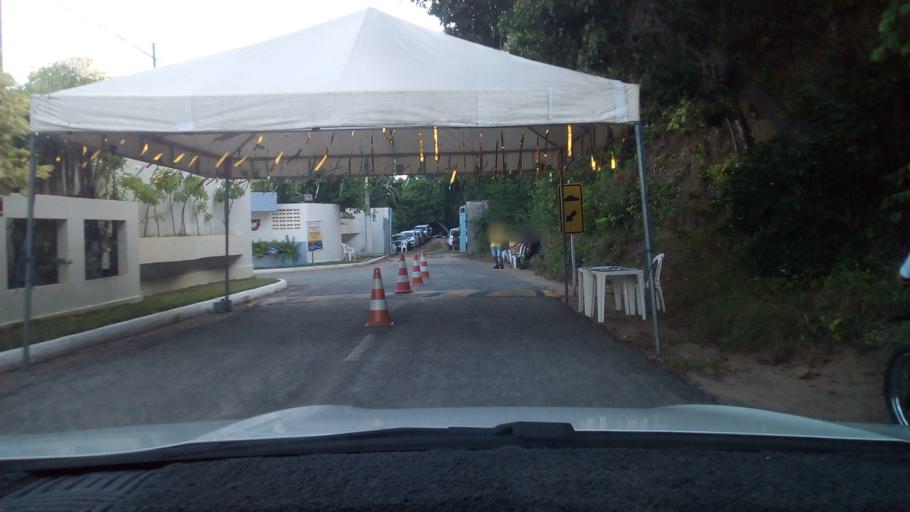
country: BR
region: Paraiba
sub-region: Joao Pessoa
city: Joao Pessoa
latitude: -7.1635
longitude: -34.7973
